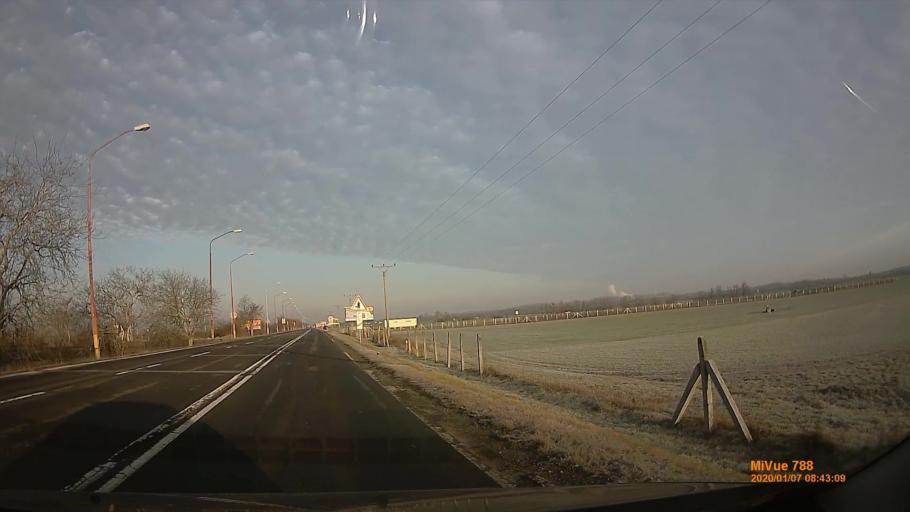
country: HU
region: Gyor-Moson-Sopron
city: Rajka
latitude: 48.0210
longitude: 17.1743
